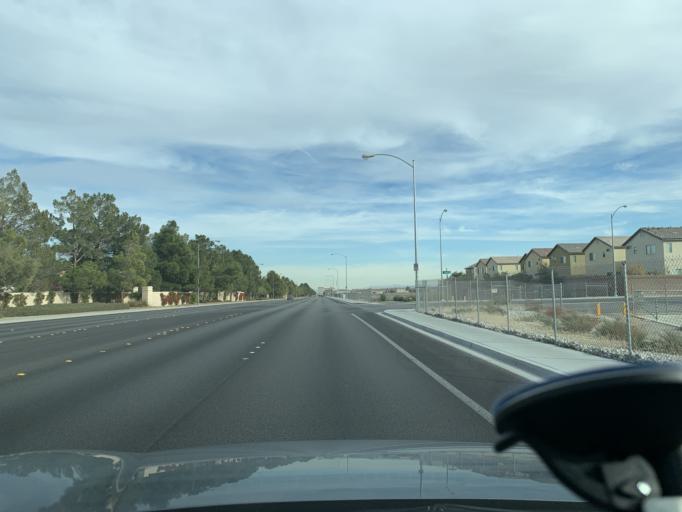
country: US
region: Nevada
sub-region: Clark County
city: Spring Valley
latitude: 36.0922
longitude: -115.2593
